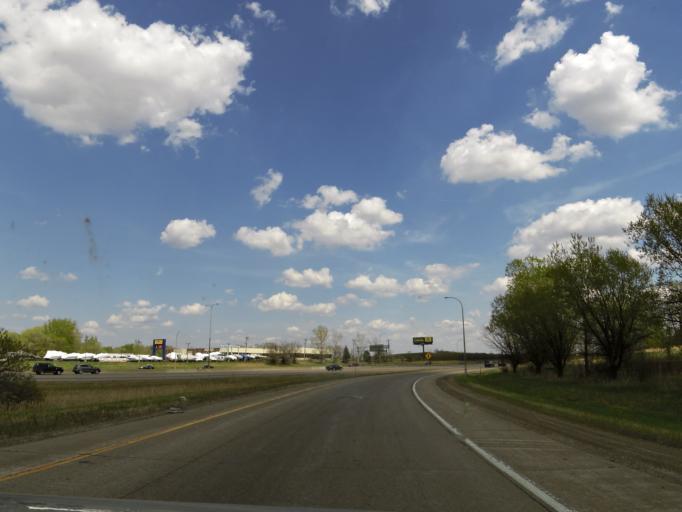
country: US
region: Minnesota
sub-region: Washington County
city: Oakdale
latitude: 44.9477
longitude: -92.9567
